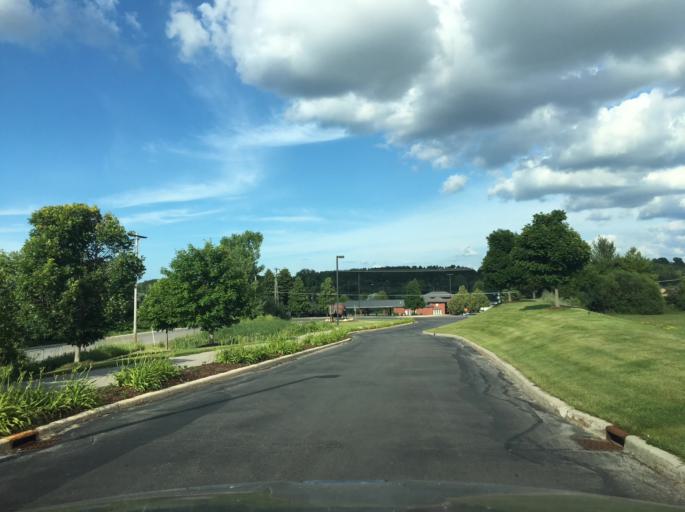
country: US
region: Michigan
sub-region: Grand Traverse County
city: Traverse City
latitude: 44.7404
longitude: -85.6469
